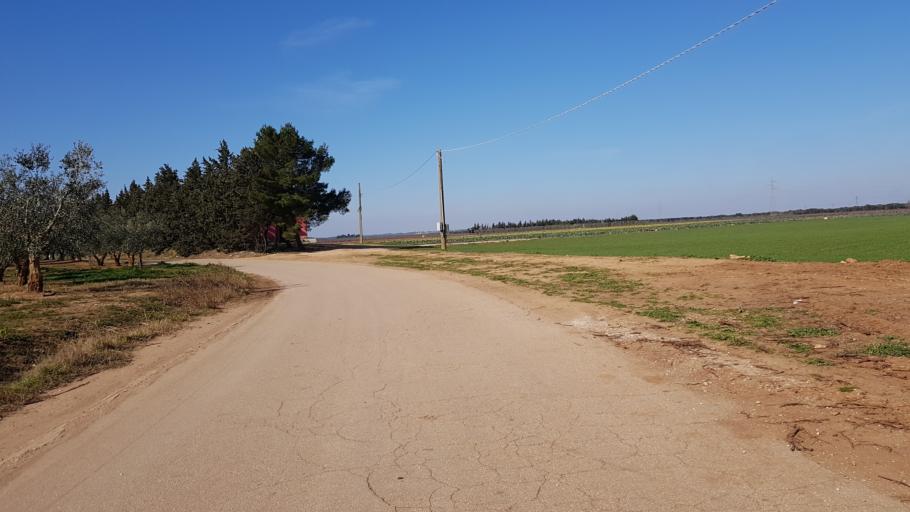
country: IT
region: Apulia
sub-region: Provincia di Brindisi
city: Mesagne
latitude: 40.6200
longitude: 17.8142
